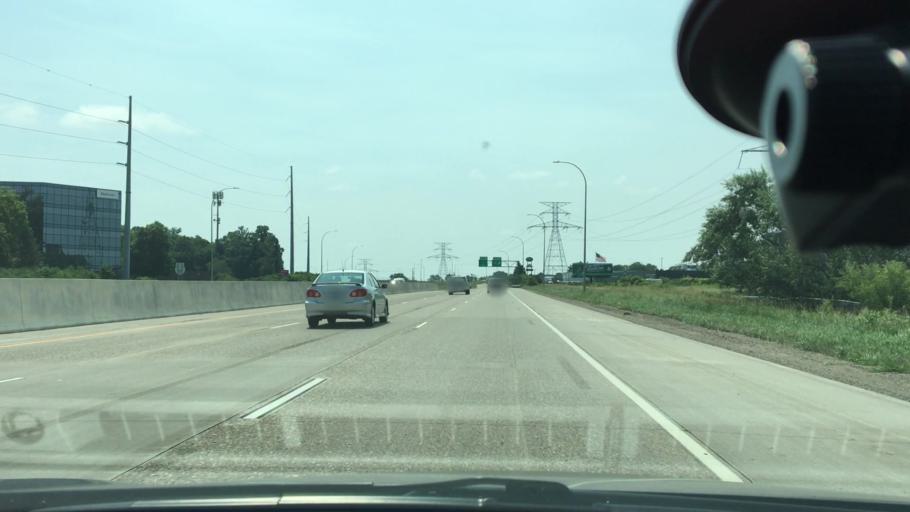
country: US
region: Minnesota
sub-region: Hennepin County
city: Plymouth
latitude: 45.0169
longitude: -93.4565
